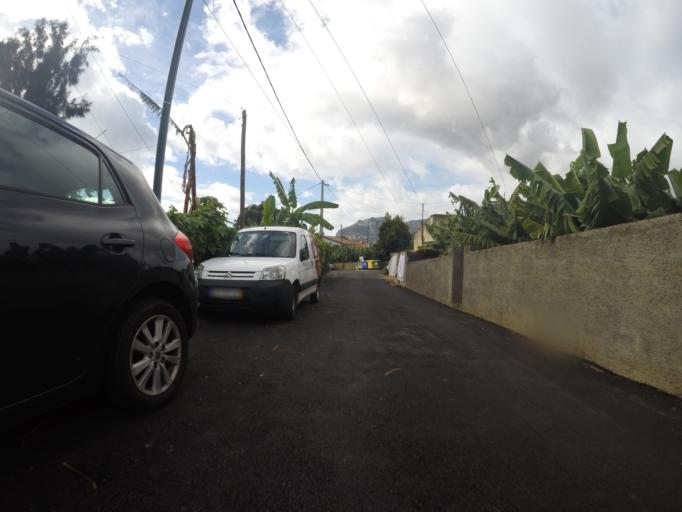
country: PT
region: Madeira
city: Camara de Lobos
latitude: 32.6497
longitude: -16.9556
